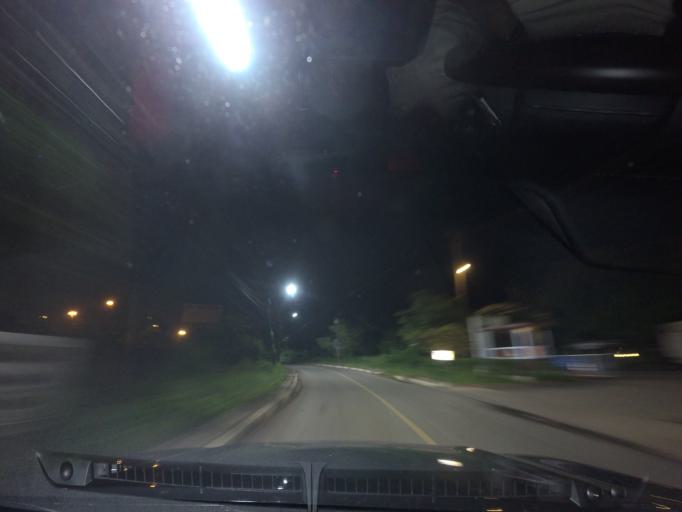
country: TH
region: Nong Khai
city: Nong Khai
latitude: 17.8668
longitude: 102.7188
